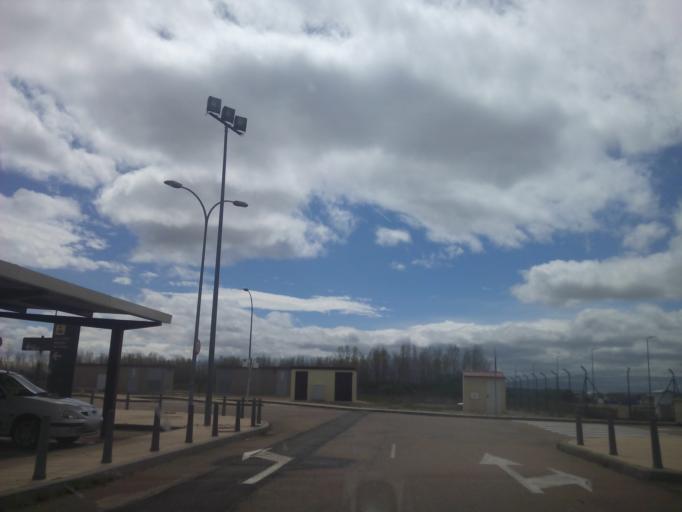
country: ES
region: Castille and Leon
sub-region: Provincia de Salamanca
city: Machacon
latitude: 40.9400
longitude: -5.5020
